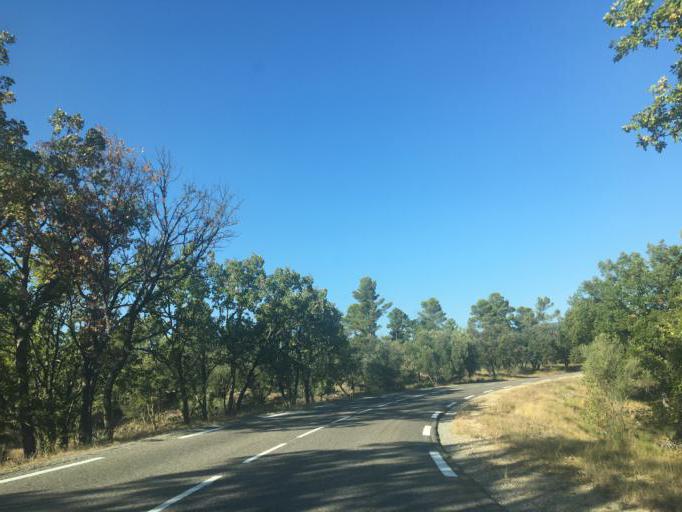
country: FR
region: Provence-Alpes-Cote d'Azur
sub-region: Departement du Var
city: Salernes
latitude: 43.5832
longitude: 6.2259
